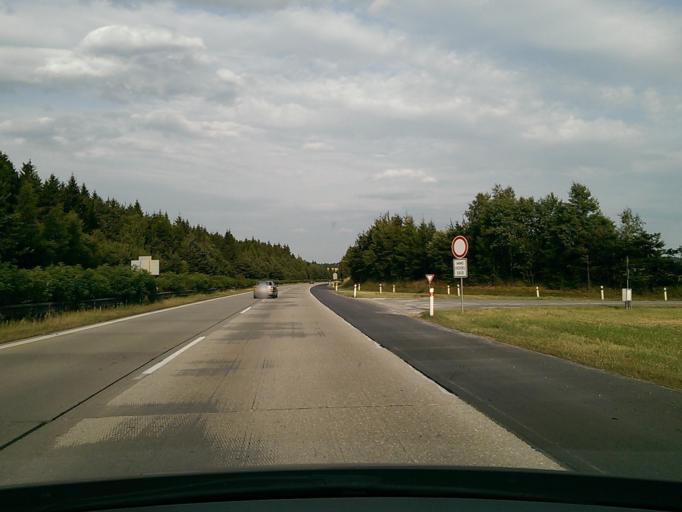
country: CZ
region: Vysocina
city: Velky Beranov
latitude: 49.4225
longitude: 15.6893
